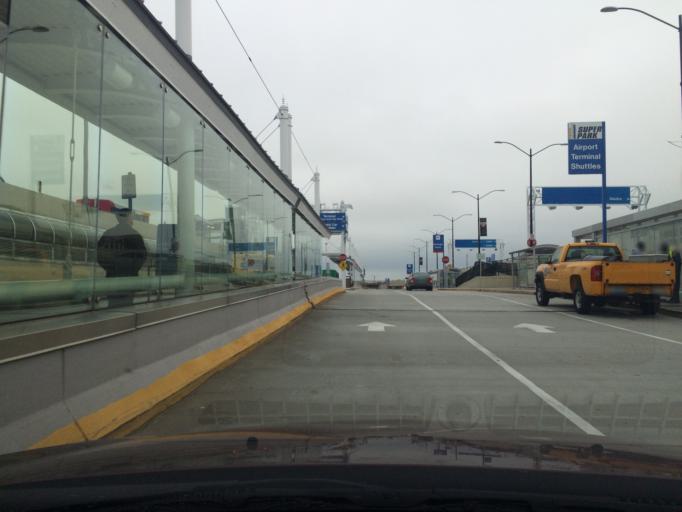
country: US
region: Missouri
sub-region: Saint Louis County
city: Woodson Terrace
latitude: 38.7420
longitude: -90.3658
